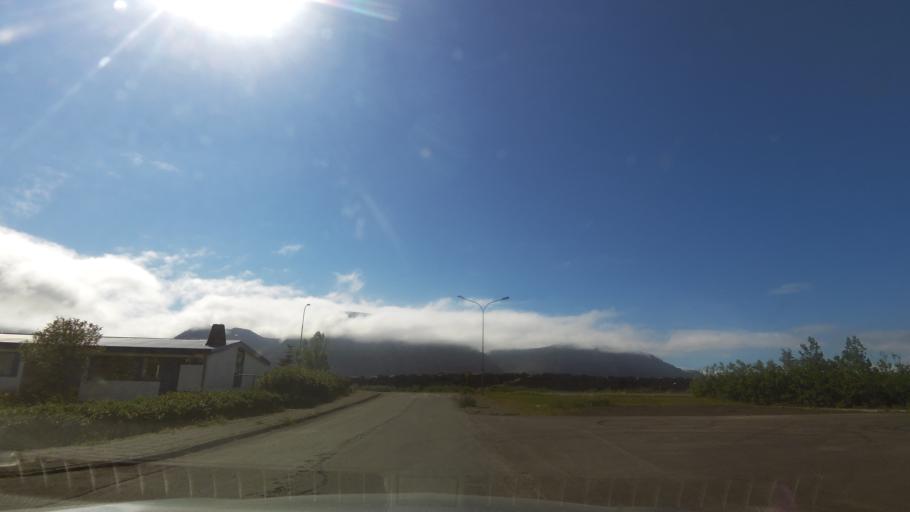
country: IS
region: Westfjords
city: Isafjoerdur
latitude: 66.0517
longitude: -23.5169
